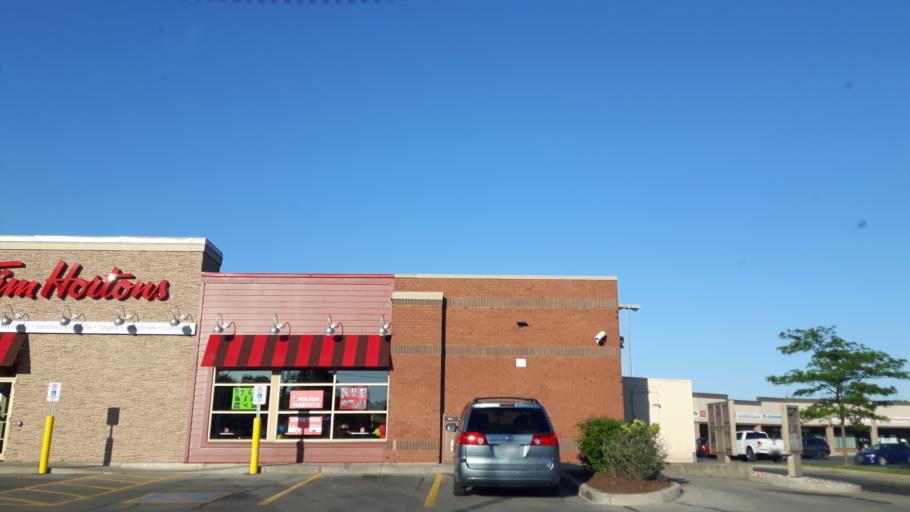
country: CA
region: Ontario
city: London
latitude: 42.9441
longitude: -81.2140
